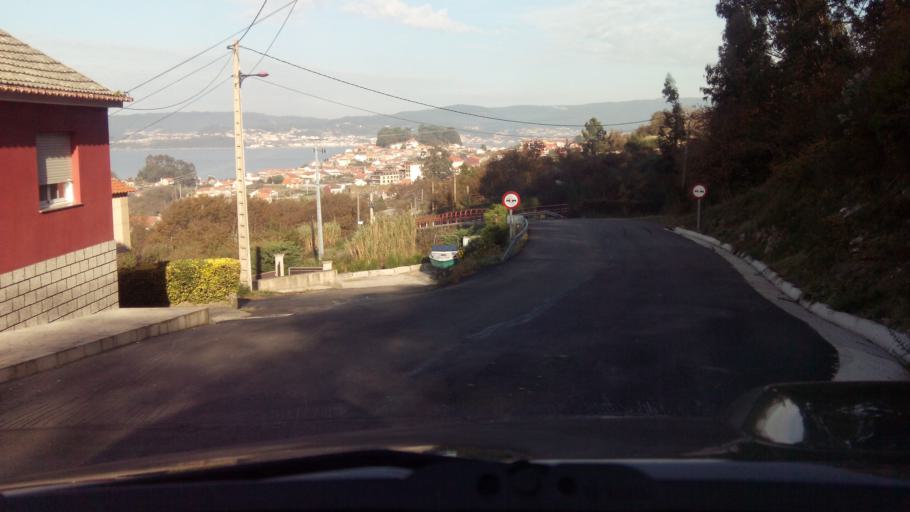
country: ES
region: Galicia
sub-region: Provincia de Pontevedra
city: Marin
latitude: 42.3594
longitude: -8.7334
